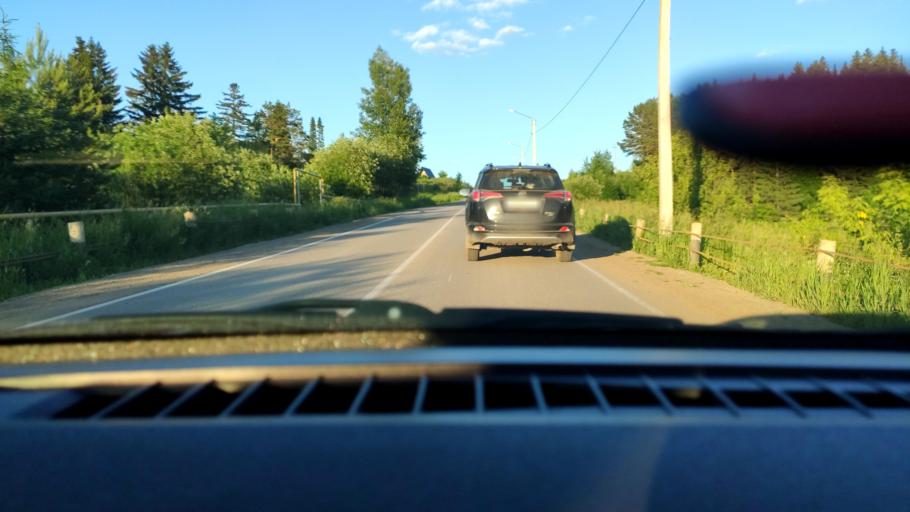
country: RU
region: Perm
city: Kultayevo
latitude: 57.9249
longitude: 55.8994
